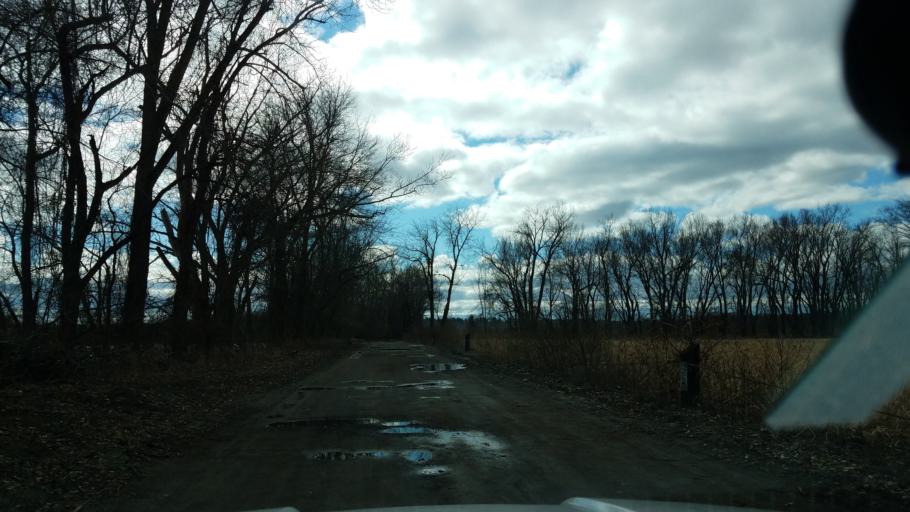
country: US
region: Connecticut
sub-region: Hartford County
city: Wethersfield
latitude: 41.6985
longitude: -72.6374
